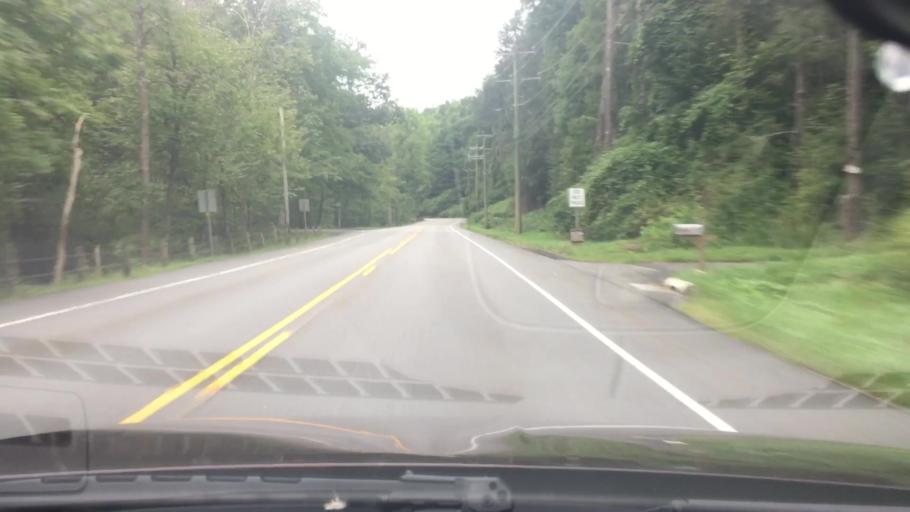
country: US
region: Connecticut
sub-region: Litchfield County
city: New Preston
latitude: 41.8275
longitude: -73.3547
